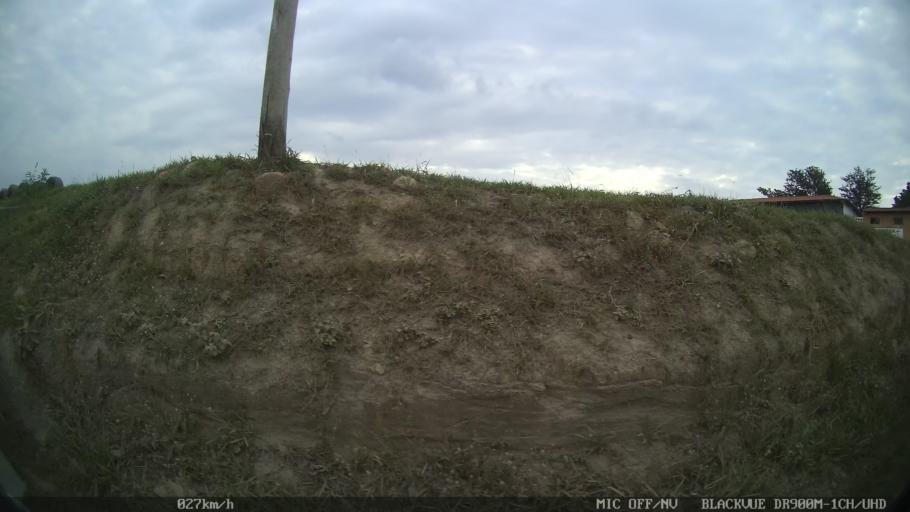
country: BR
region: Sao Paulo
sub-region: Santa Barbara D'Oeste
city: Santa Barbara d'Oeste
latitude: -22.6836
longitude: -47.3887
